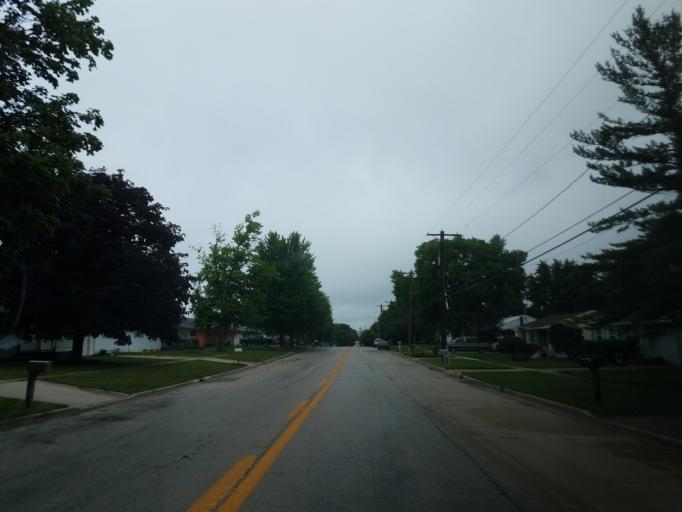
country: US
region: Illinois
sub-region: McLean County
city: Bloomington
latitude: 40.4641
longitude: -88.9817
